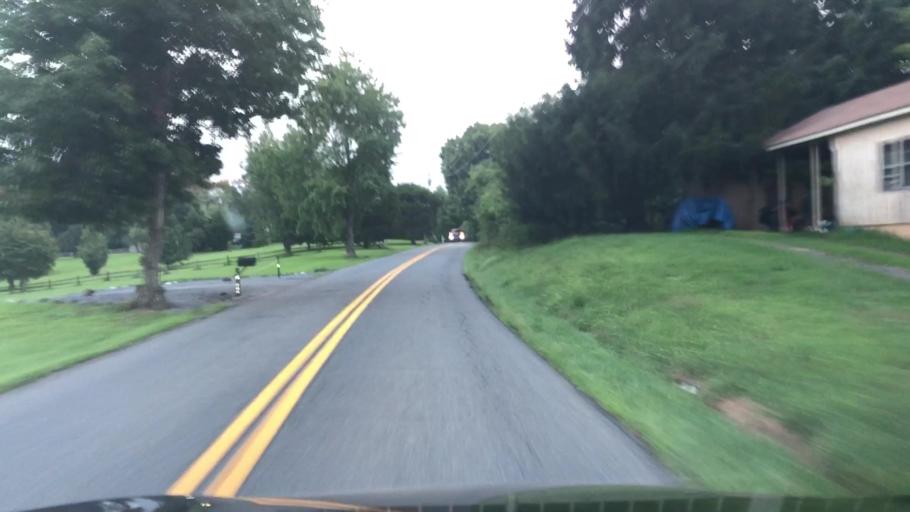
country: US
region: Virginia
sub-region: Stafford County
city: Stafford
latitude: 38.4865
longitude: -77.5795
